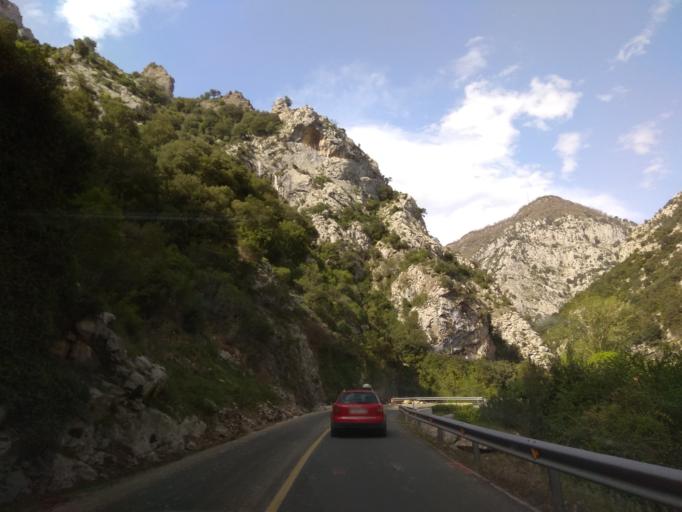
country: ES
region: Cantabria
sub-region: Provincia de Cantabria
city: Potes
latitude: 43.2271
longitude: -4.5836
